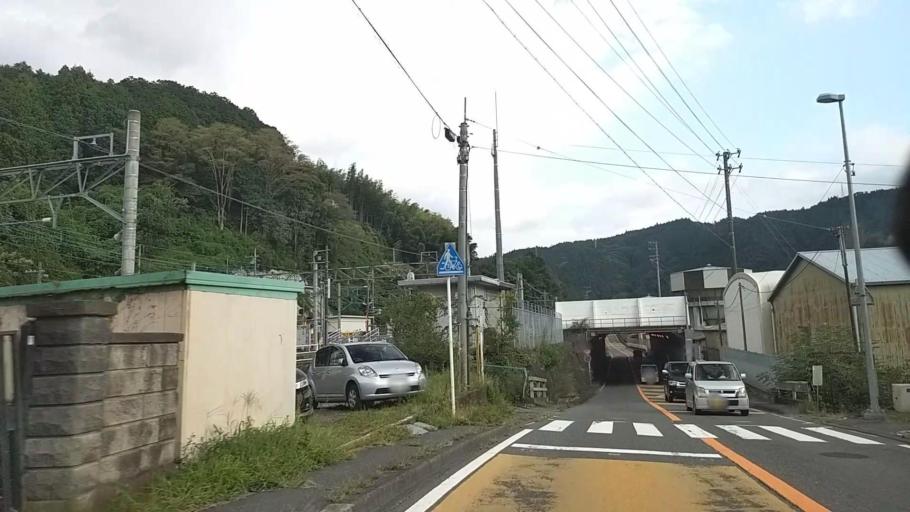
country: JP
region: Shizuoka
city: Fujinomiya
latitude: 35.1982
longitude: 138.5629
